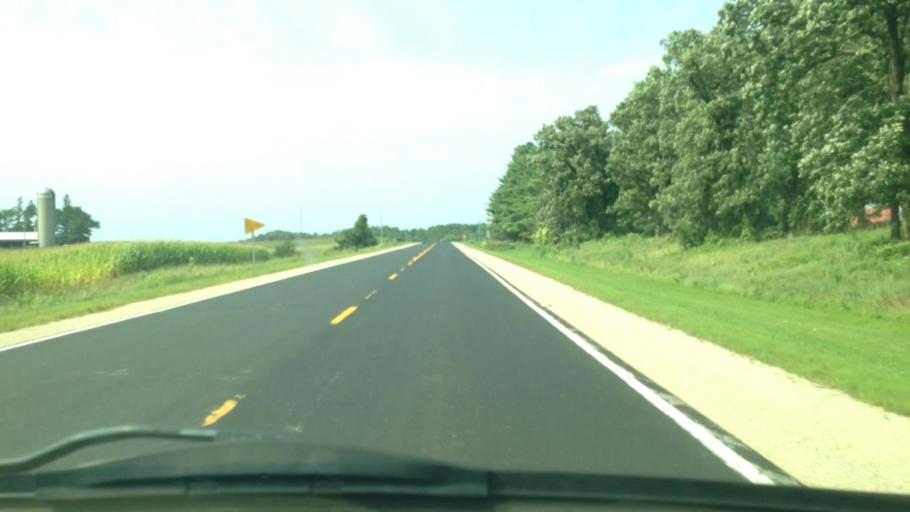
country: US
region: Minnesota
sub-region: Winona County
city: Lewiston
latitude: 43.9167
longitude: -91.9593
